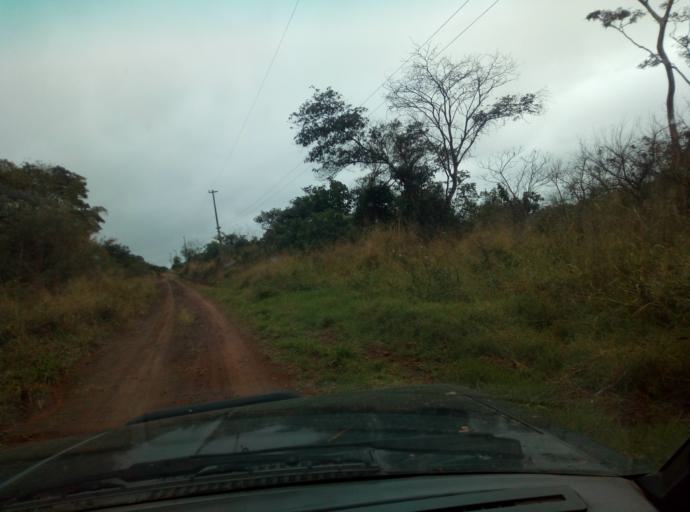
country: PY
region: Caaguazu
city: Carayao
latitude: -25.1904
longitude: -56.3545
